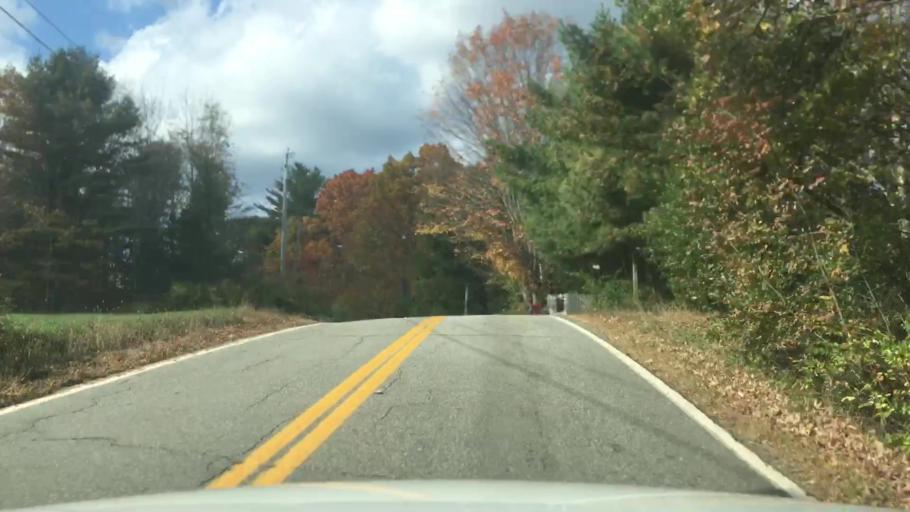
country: US
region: Maine
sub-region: Knox County
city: Washington
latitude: 44.3107
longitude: -69.3475
